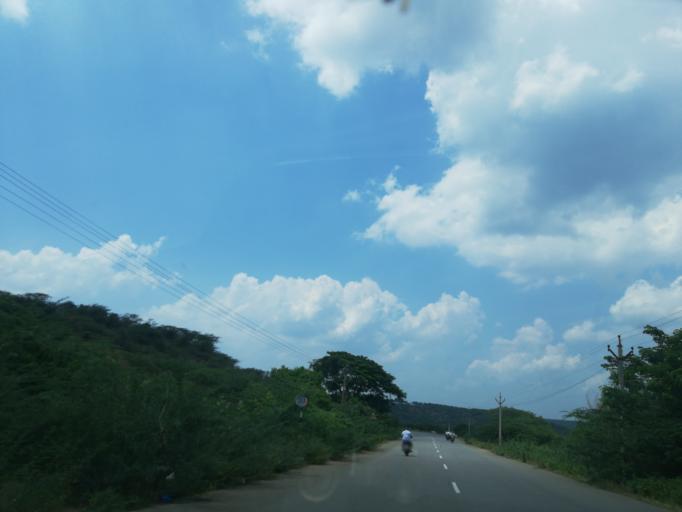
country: IN
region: Andhra Pradesh
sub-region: Guntur
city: Macherla
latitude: 16.5942
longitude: 79.3148
